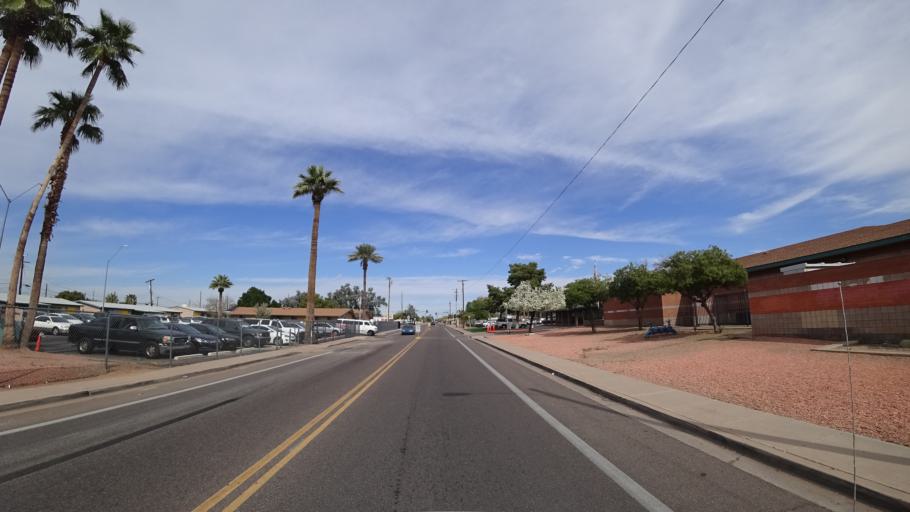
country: US
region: Arizona
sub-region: Maricopa County
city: Phoenix
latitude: 33.4642
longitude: -112.1258
